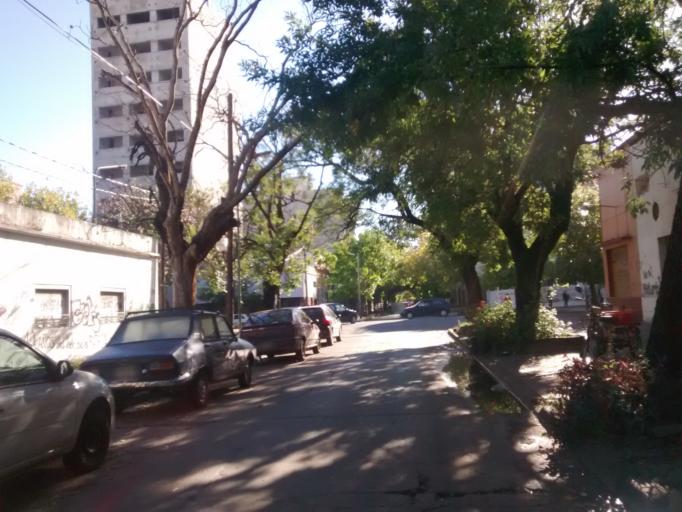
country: AR
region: Buenos Aires
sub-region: Partido de La Plata
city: La Plata
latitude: -34.9294
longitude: -57.9447
